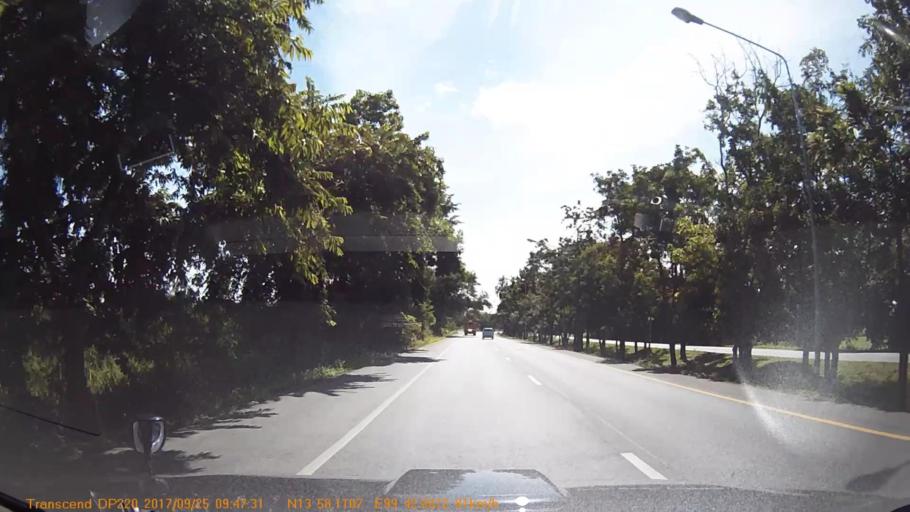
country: TH
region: Kanchanaburi
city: Tha Maka
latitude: 13.9685
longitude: 99.7138
